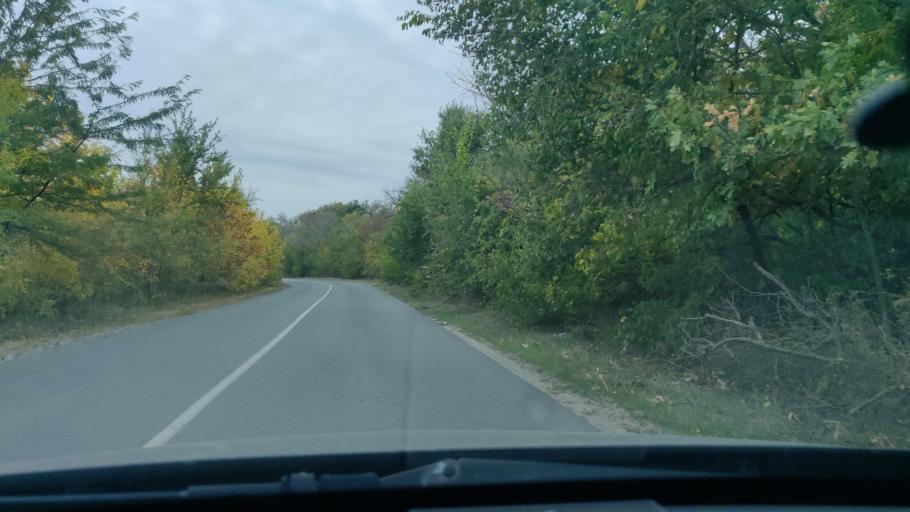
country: RU
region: Rostov
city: Ust'-Donetskiy
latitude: 47.6540
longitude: 40.8943
